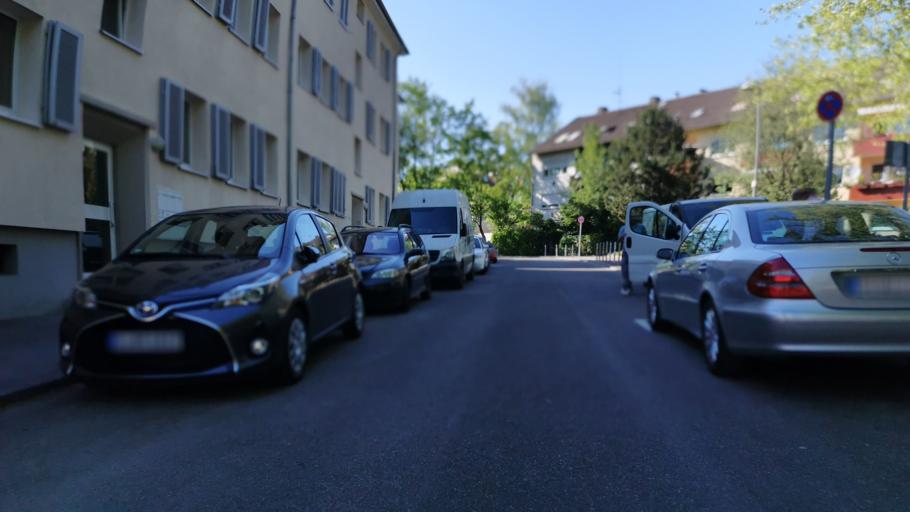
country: DE
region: Baden-Wuerttemberg
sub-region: Regierungsbezirk Stuttgart
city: Stuttgart Muehlhausen
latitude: 48.8162
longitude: 9.2143
